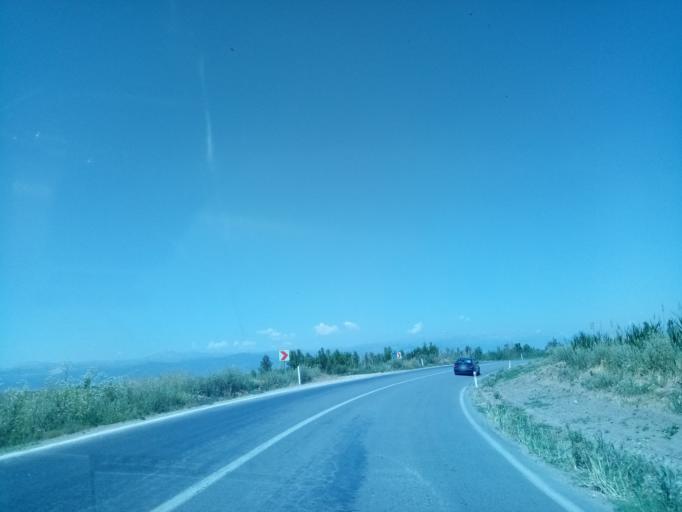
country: TR
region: Konya
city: Yalihuyuk
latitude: 37.3832
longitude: 32.0544
